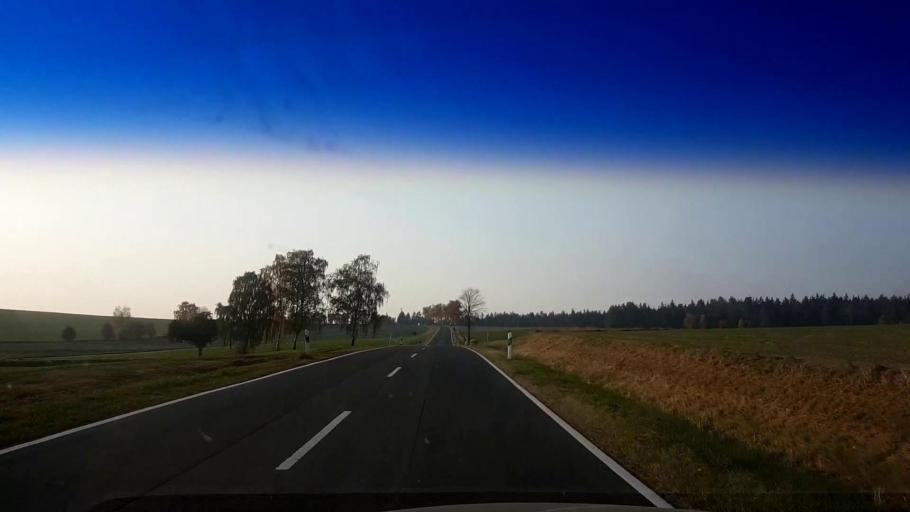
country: DE
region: Bavaria
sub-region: Upper Palatinate
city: Waldsassen
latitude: 50.0419
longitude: 12.2879
